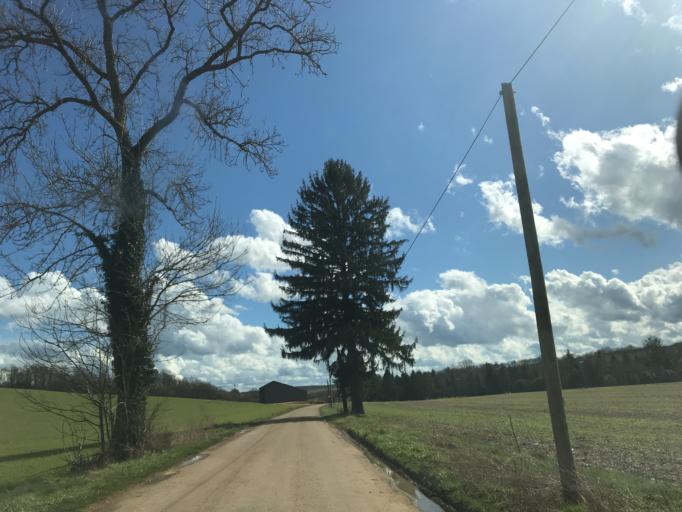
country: FR
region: Bourgogne
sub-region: Departement de l'Yonne
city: Fontenailles
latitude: 47.5148
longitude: 3.4957
